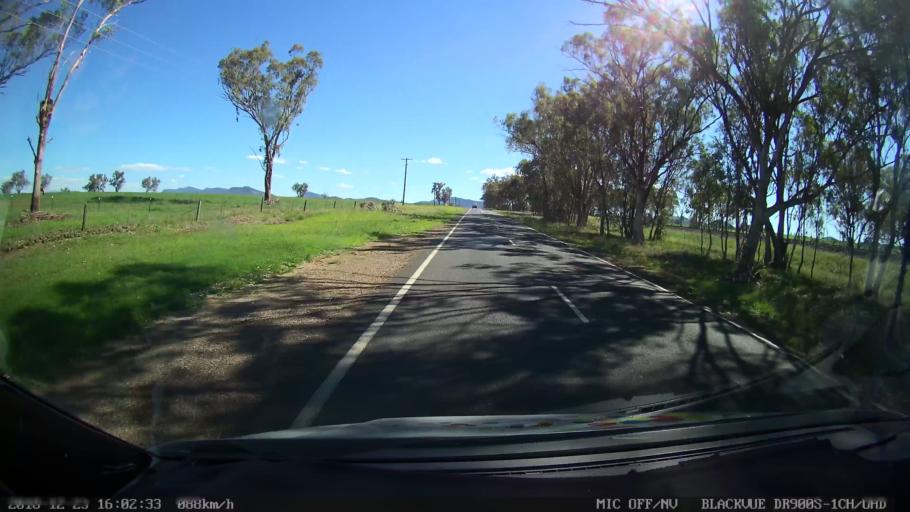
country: AU
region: New South Wales
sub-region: Tamworth Municipality
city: Phillip
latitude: -31.2336
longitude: 150.8081
